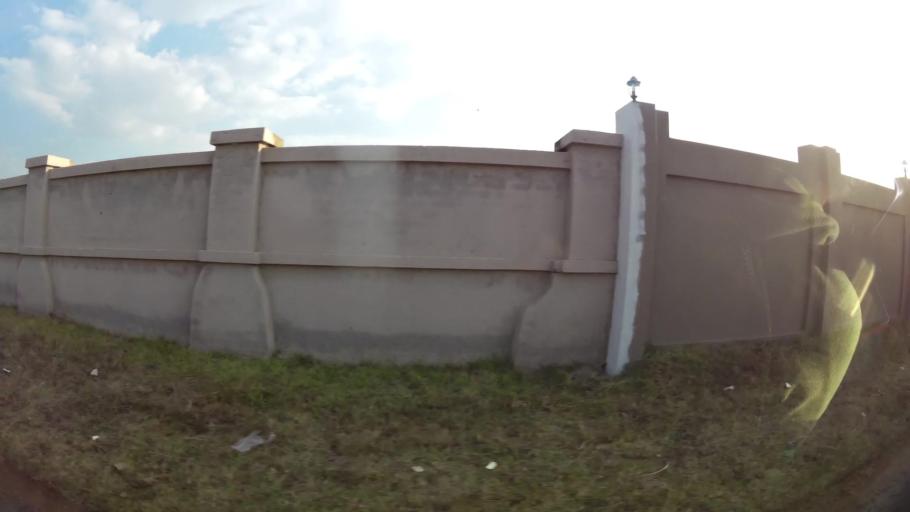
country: ZA
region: Gauteng
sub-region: Ekurhuleni Metropolitan Municipality
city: Benoni
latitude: -26.1267
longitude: 28.2916
